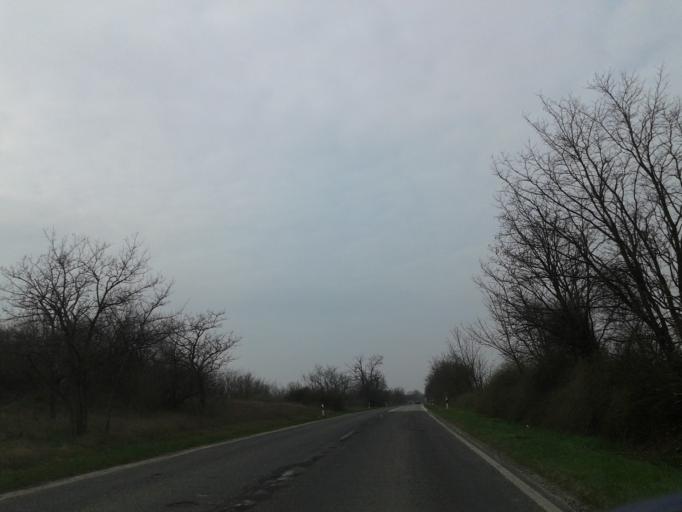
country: HU
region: Komarom-Esztergom
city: Komarom
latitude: 47.7354
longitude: 18.0702
